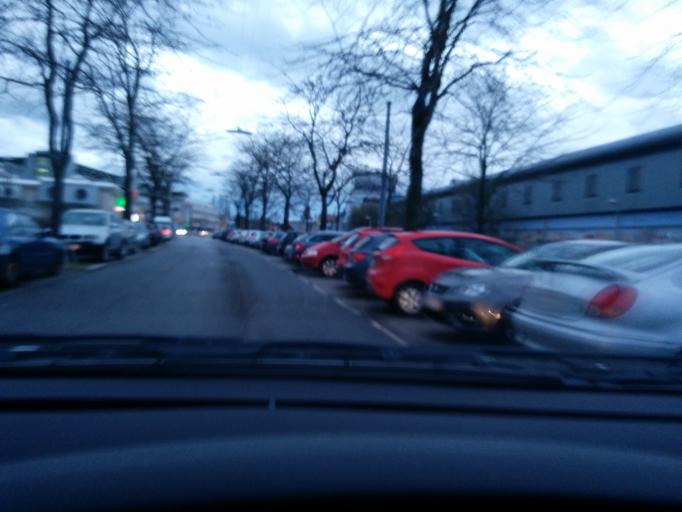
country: AT
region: Lower Austria
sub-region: Politischer Bezirk Modling
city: Vosendorf
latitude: 48.1307
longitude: 16.3103
